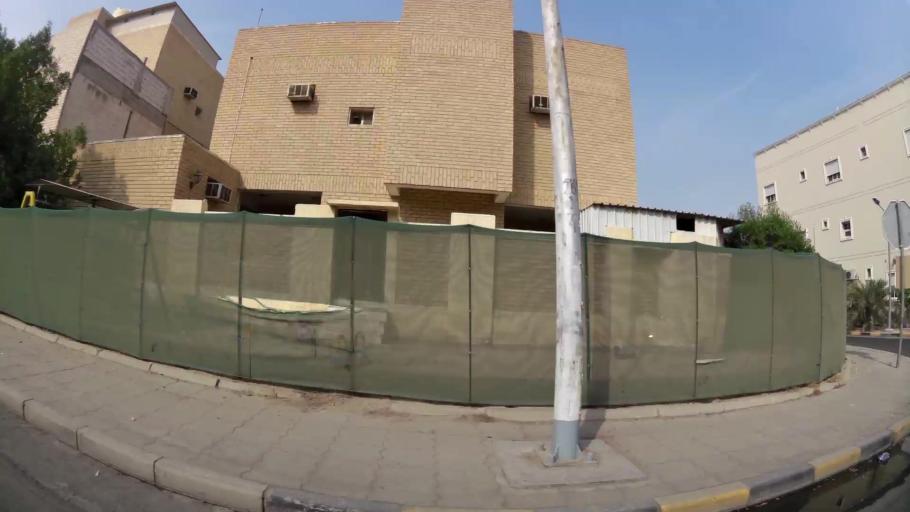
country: KW
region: Al Asimah
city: Ar Rabiyah
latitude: 29.2838
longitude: 47.9417
